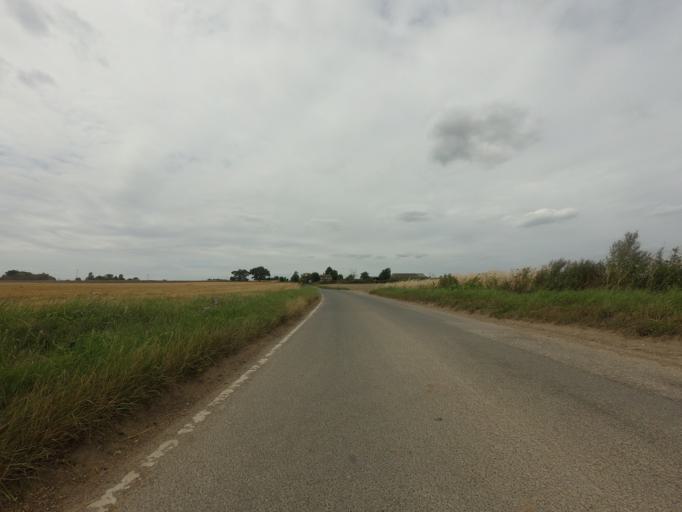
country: GB
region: England
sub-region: Medway
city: Stoke
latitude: 51.4367
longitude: 0.6092
